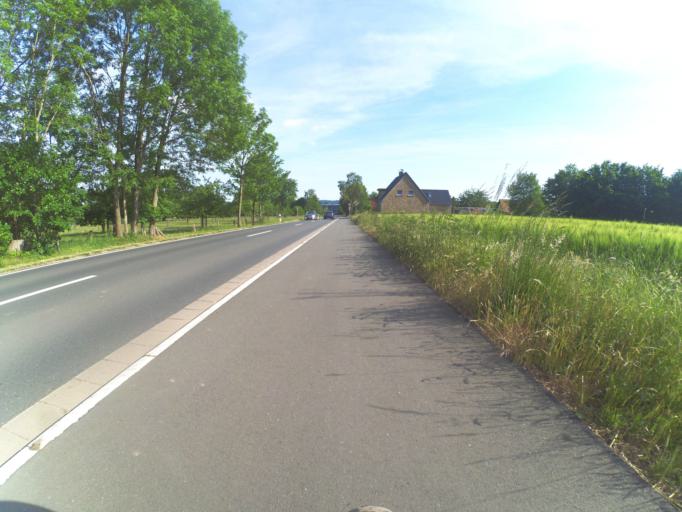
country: DE
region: North Rhine-Westphalia
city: Ibbenburen
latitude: 52.2744
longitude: 7.7489
